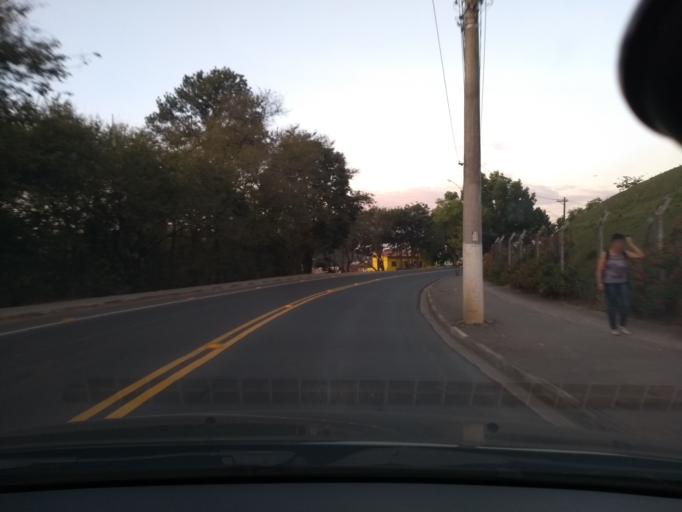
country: BR
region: Sao Paulo
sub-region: Itupeva
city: Itupeva
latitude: -23.1423
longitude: -47.0424
